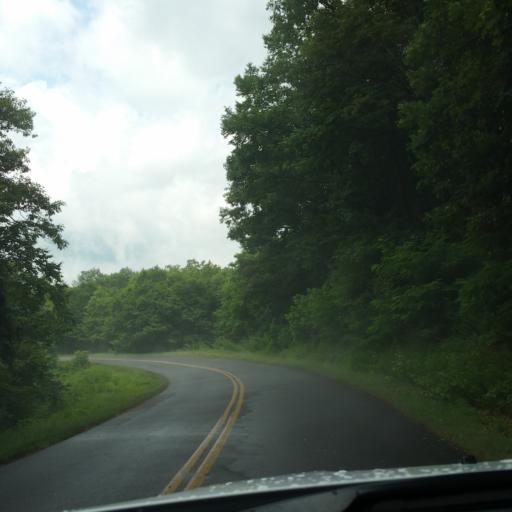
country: US
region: North Carolina
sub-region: Transylvania County
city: Brevard
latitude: 35.3470
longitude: -82.8062
